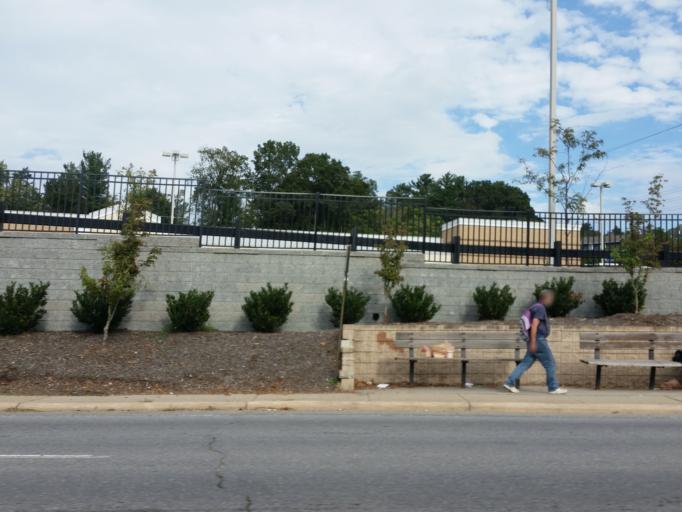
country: US
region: North Carolina
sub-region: Buncombe County
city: Asheville
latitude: 35.6300
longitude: -82.5528
